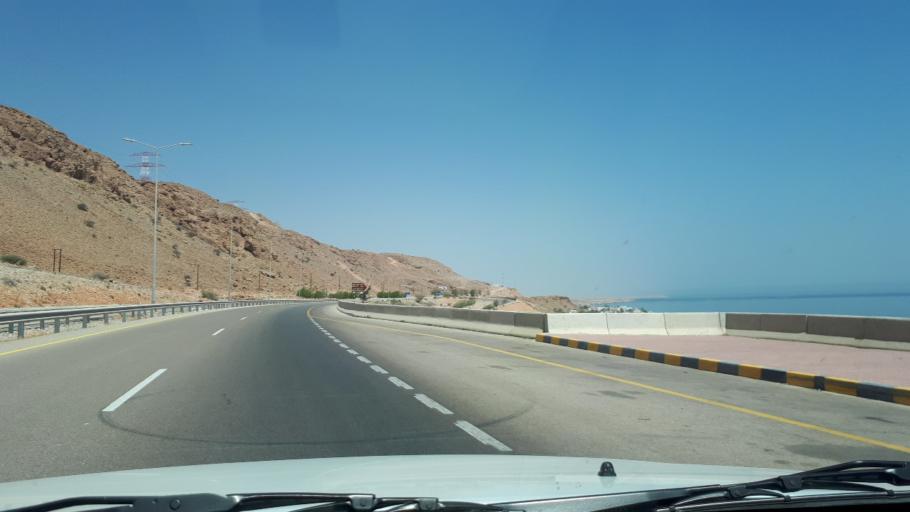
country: OM
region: Ash Sharqiyah
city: Sur
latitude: 22.8258
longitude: 59.2545
